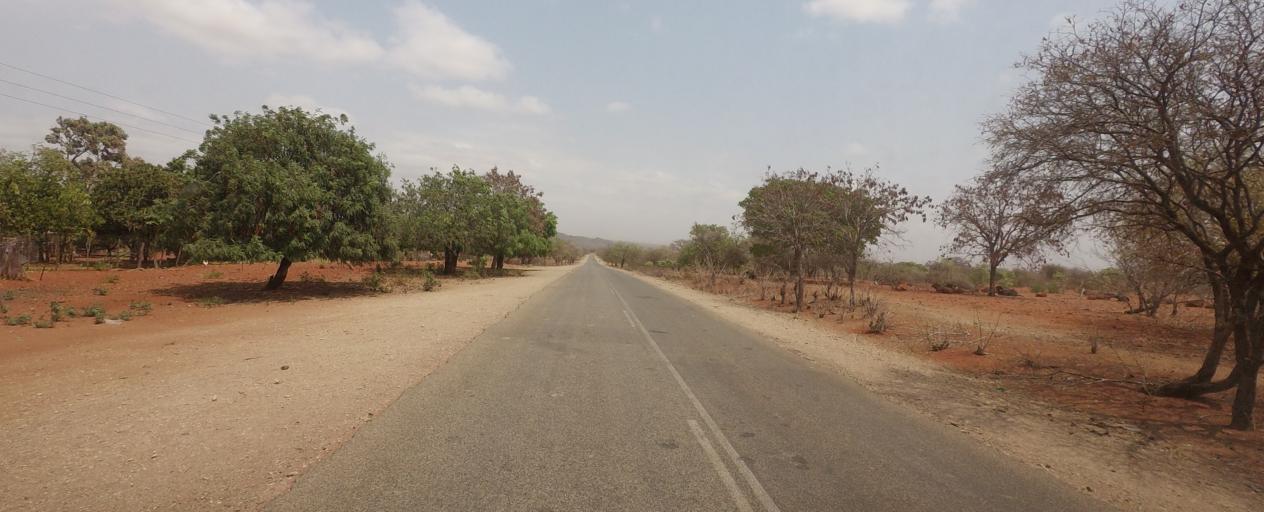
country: ZA
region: Limpopo
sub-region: Vhembe District Municipality
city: Mutale
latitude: -22.4227
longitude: 30.8956
